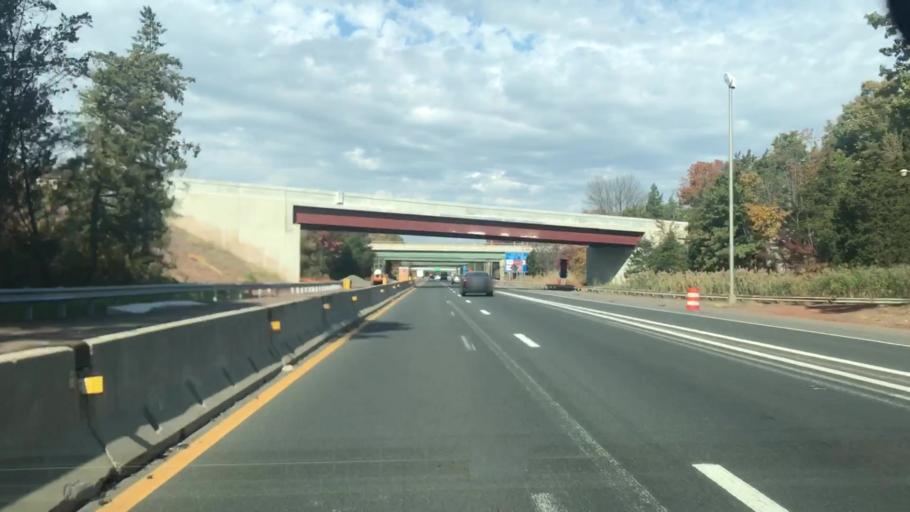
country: US
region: New Jersey
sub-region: Somerset County
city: Bedminster
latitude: 40.6410
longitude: -74.6447
